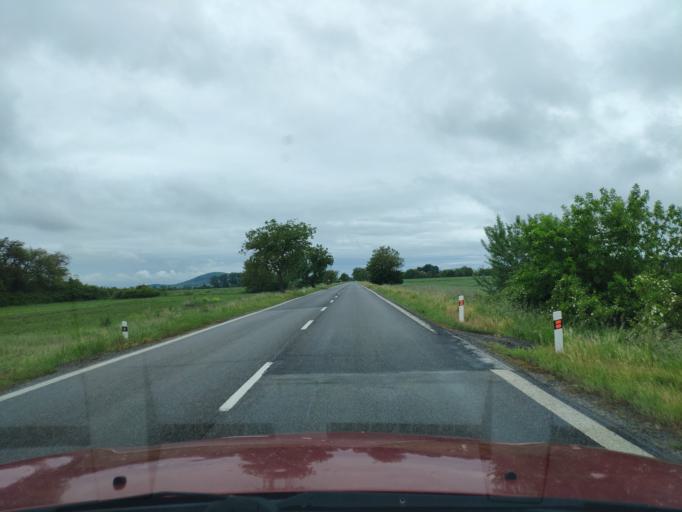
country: HU
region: Borsod-Abauj-Zemplen
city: Karcsa
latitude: 48.4185
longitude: 21.8329
